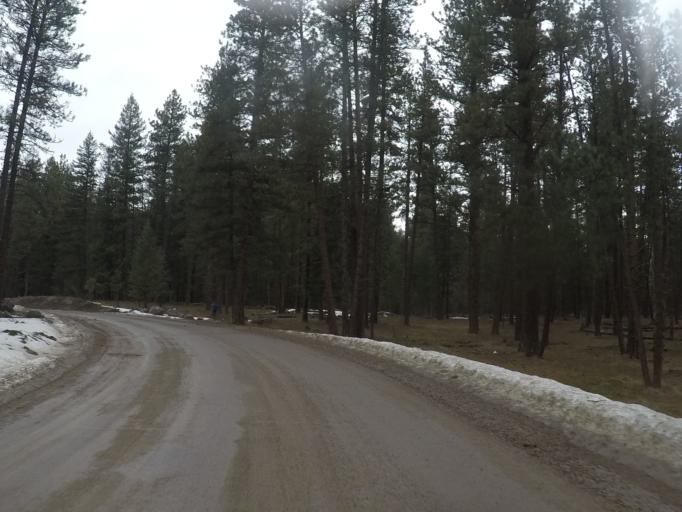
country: US
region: Montana
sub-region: Missoula County
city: East Missoula
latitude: 46.9223
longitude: -113.9591
